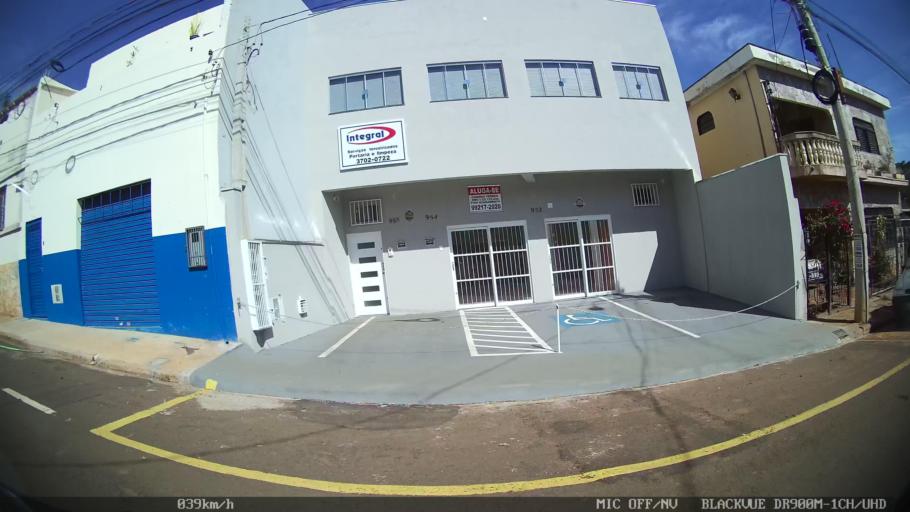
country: BR
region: Sao Paulo
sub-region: Franca
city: Franca
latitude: -20.5347
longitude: -47.4057
